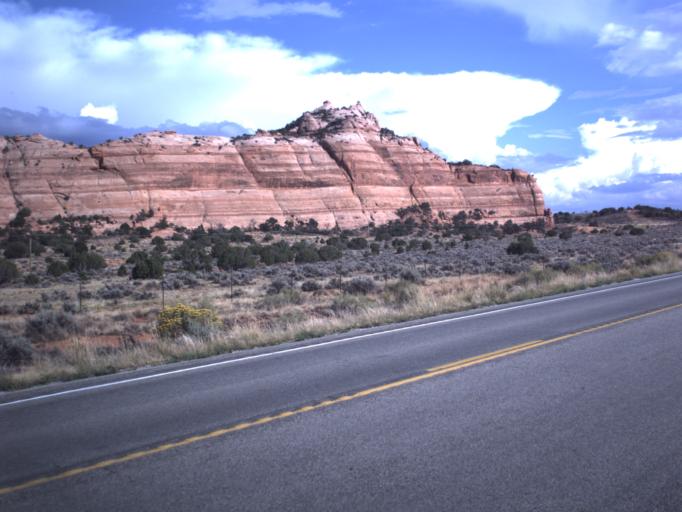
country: US
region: Utah
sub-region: Grand County
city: Moab
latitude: 38.3325
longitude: -109.4309
